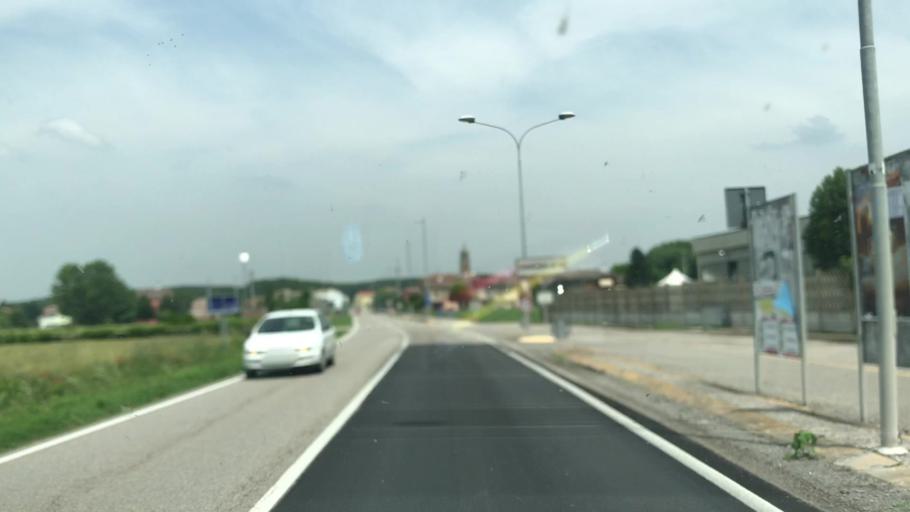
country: IT
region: Lombardy
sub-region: Provincia di Mantova
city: Carbonara di Po
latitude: 45.0331
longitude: 11.2251
